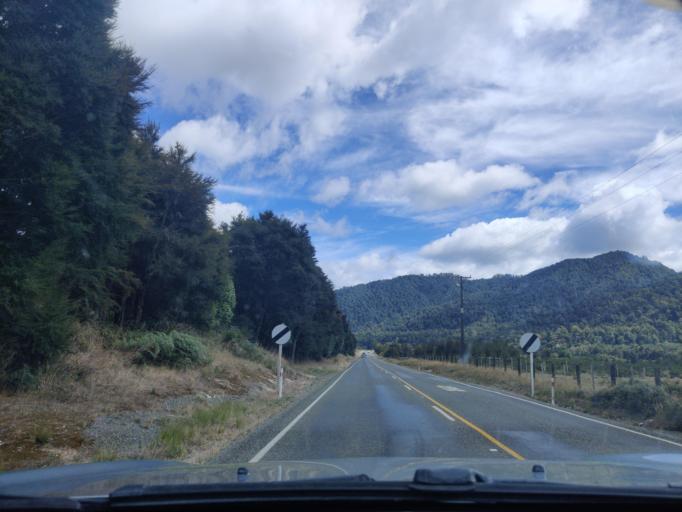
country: NZ
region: Tasman
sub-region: Tasman District
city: Wakefield
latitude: -41.7042
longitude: 172.5363
